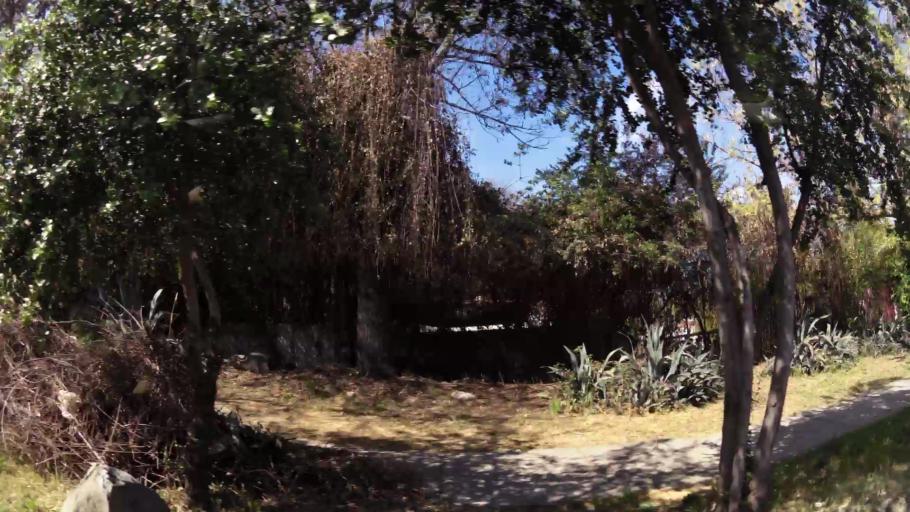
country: CL
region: Santiago Metropolitan
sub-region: Provincia de Santiago
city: Villa Presidente Frei, Nunoa, Santiago, Chile
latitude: -33.4358
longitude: -70.5239
